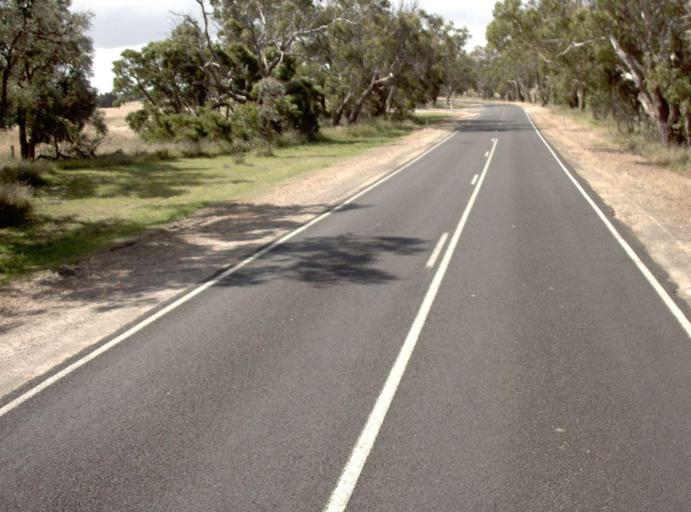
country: AU
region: Victoria
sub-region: Wellington
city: Sale
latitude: -38.2896
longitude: 147.1554
